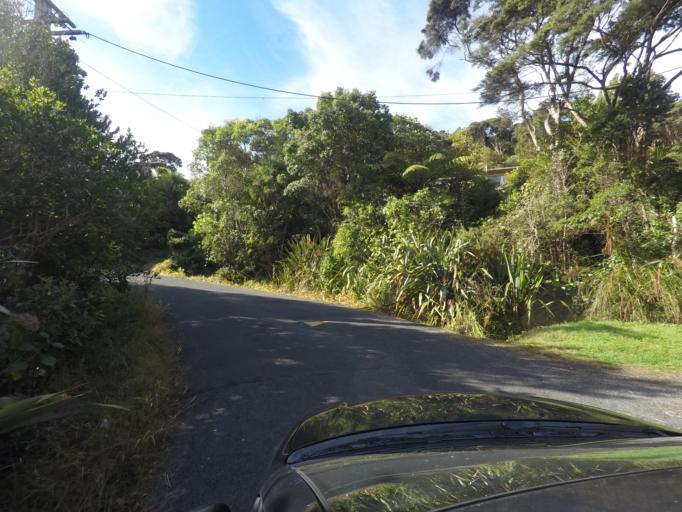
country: NZ
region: Auckland
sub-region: Auckland
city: Titirangi
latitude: -36.9971
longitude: 174.5762
